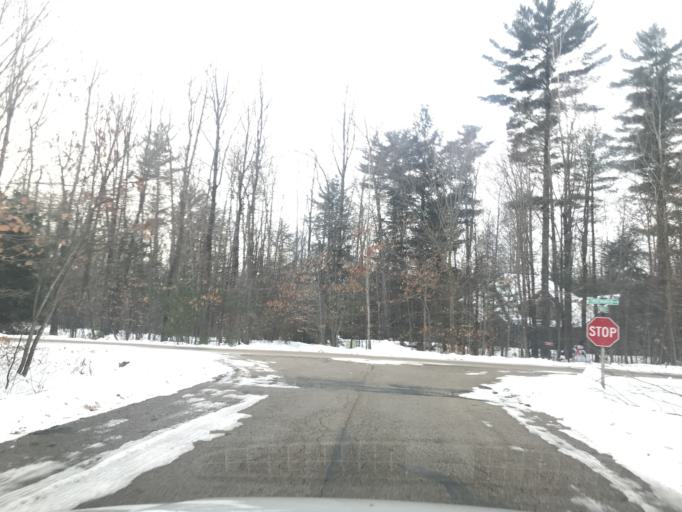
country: US
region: Wisconsin
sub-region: Brown County
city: Suamico
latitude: 44.6861
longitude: -88.0605
